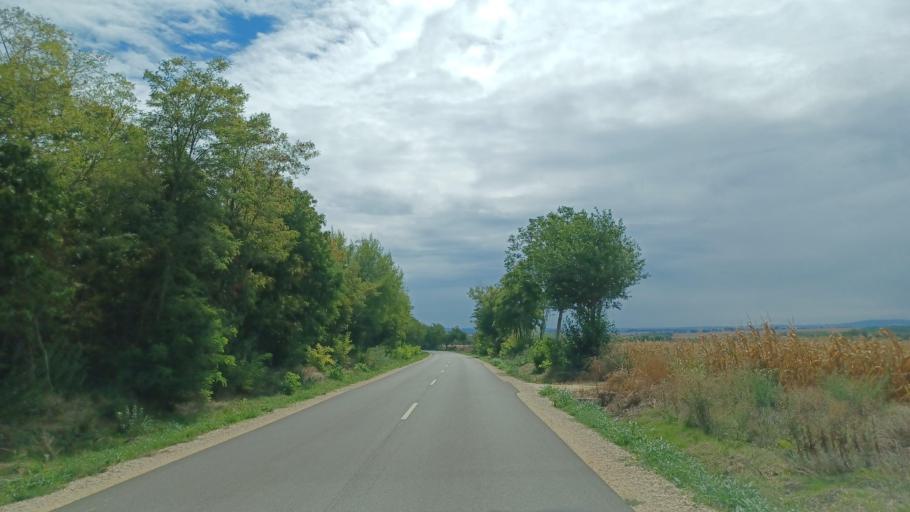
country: HU
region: Tolna
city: Zomba
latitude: 46.4674
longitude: 18.5962
